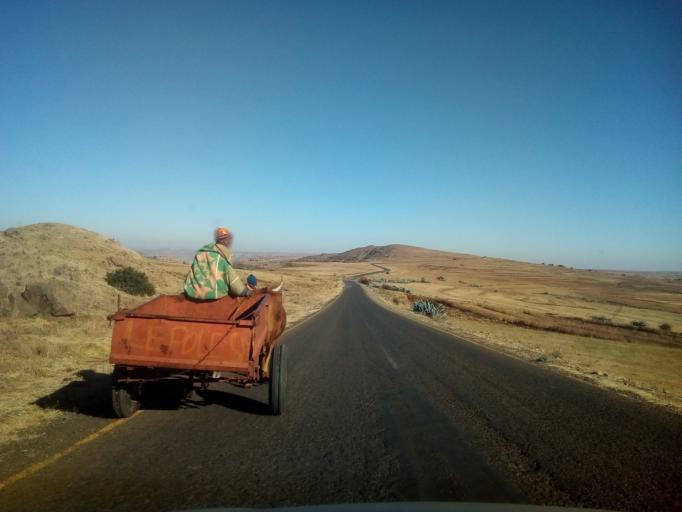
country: LS
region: Berea
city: Teyateyaneng
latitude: -29.2536
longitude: 27.7844
